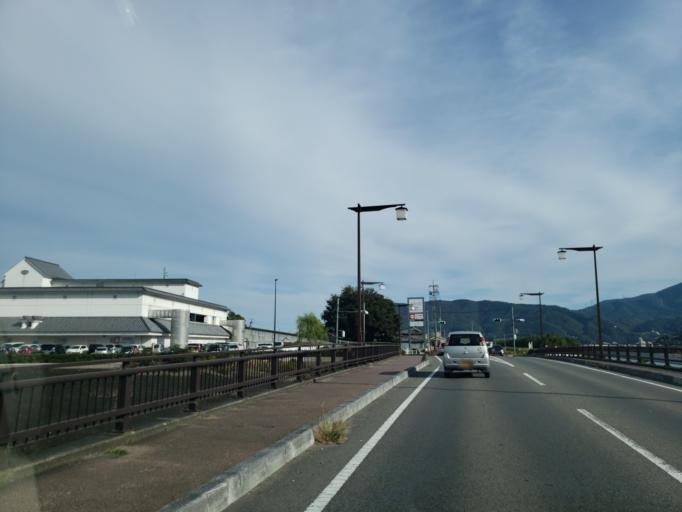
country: JP
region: Tokushima
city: Wakimachi
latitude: 34.0661
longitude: 134.1482
